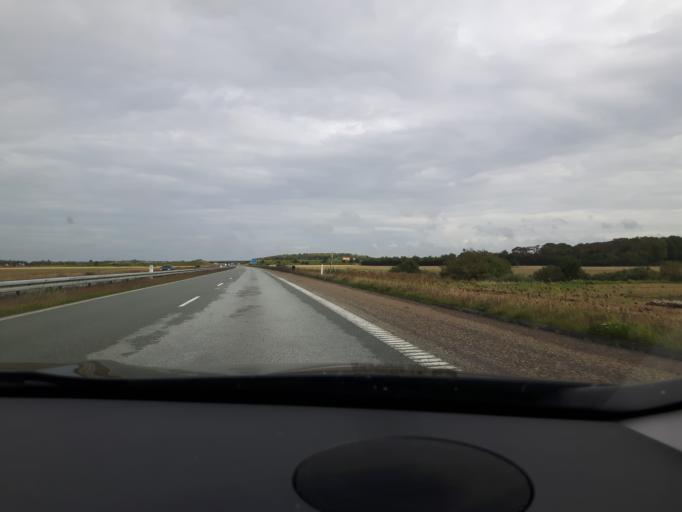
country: DK
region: North Denmark
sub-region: Hjorring Kommune
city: Hjorring
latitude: 57.4413
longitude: 10.0392
